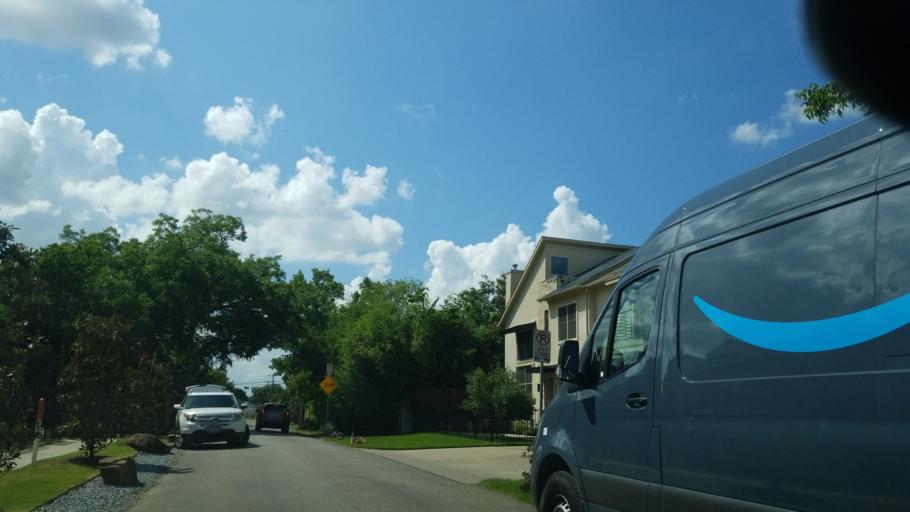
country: US
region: Texas
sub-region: Dallas County
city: Highland Park
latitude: 32.8280
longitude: -96.8207
